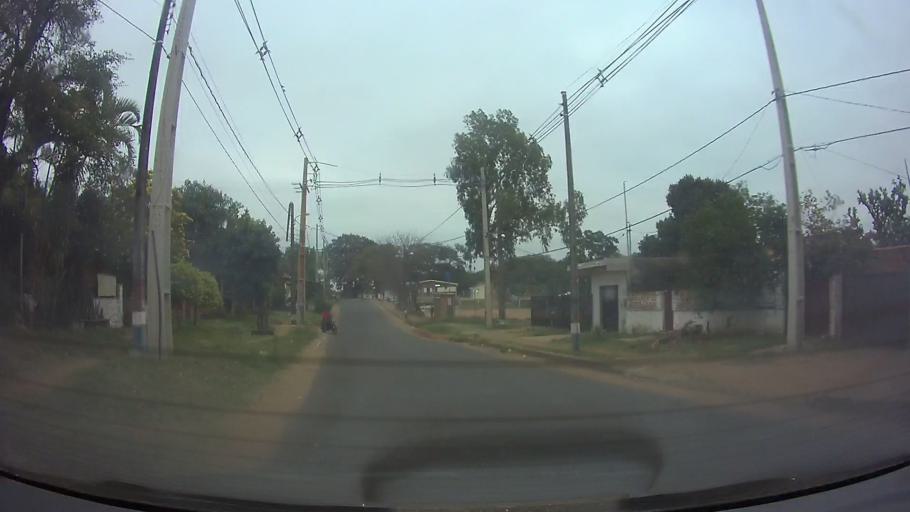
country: PY
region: Central
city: Limpio
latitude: -25.1504
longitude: -57.4581
